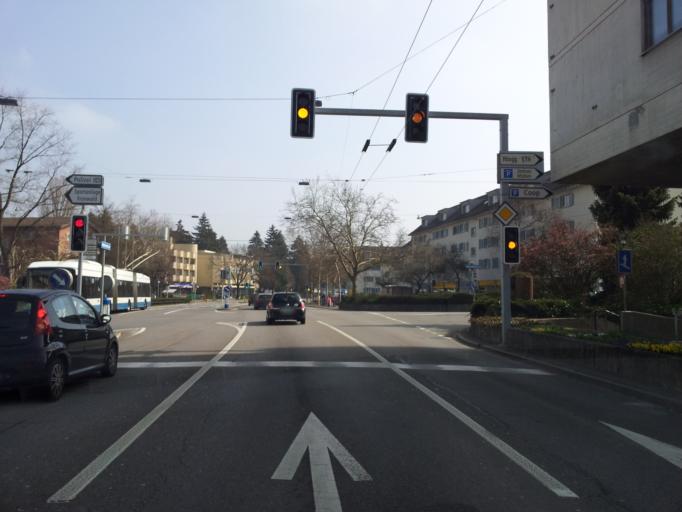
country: CH
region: Zurich
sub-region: Bezirk Zuerich
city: Zuerich (Kreis 11) / Affoltern
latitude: 47.4192
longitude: 8.5057
